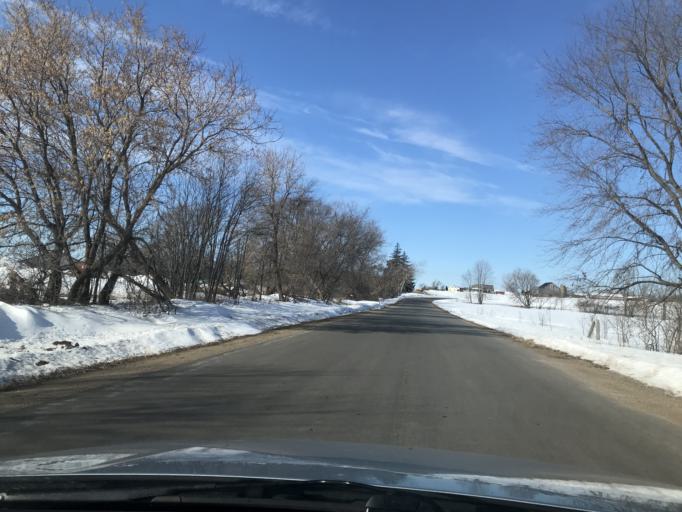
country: US
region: Wisconsin
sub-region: Oconto County
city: Gillett
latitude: 44.9397
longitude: -88.2633
